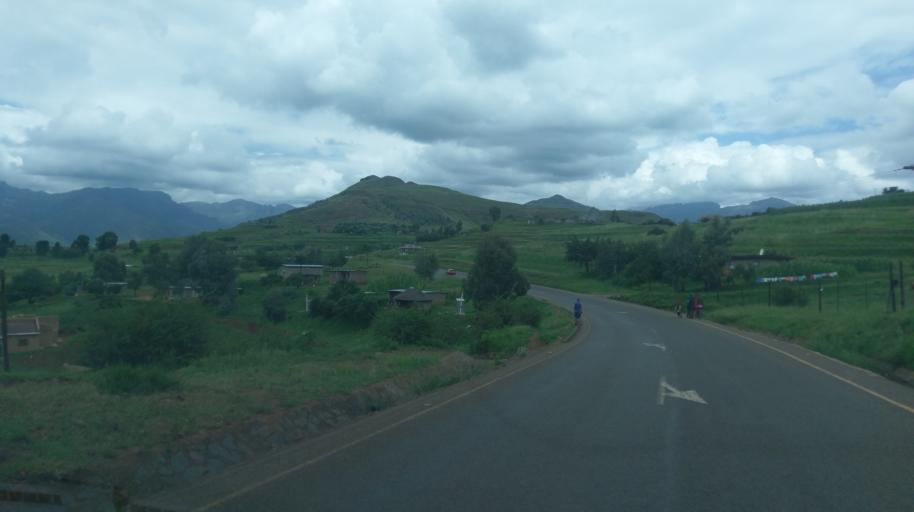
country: LS
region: Leribe
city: Leribe
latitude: -29.0168
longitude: 28.2183
